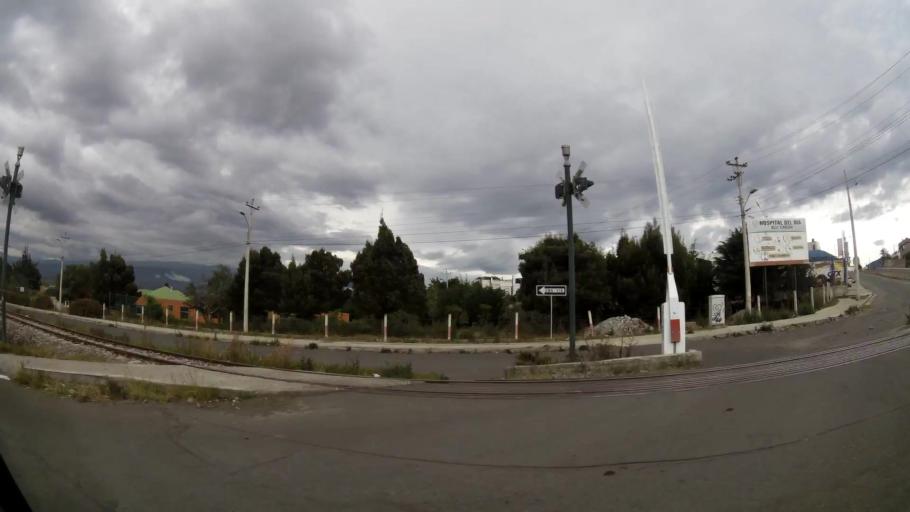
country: EC
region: Tungurahua
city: Ambato
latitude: -1.2783
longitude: -78.6191
